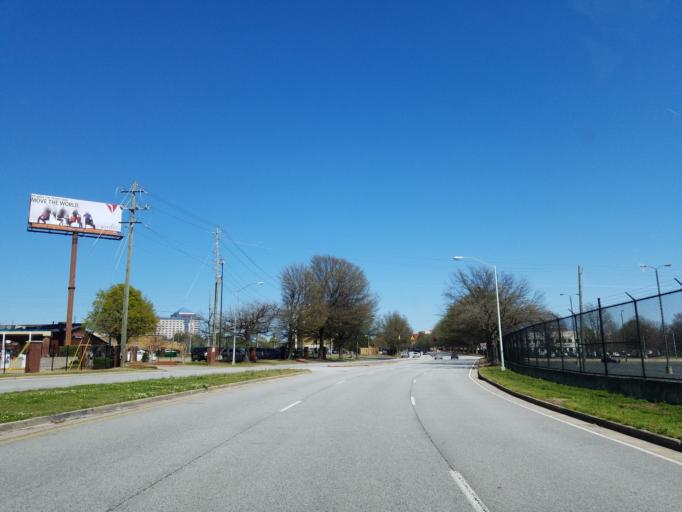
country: US
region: Georgia
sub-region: Fulton County
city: College Park
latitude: 33.6576
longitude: -84.4314
